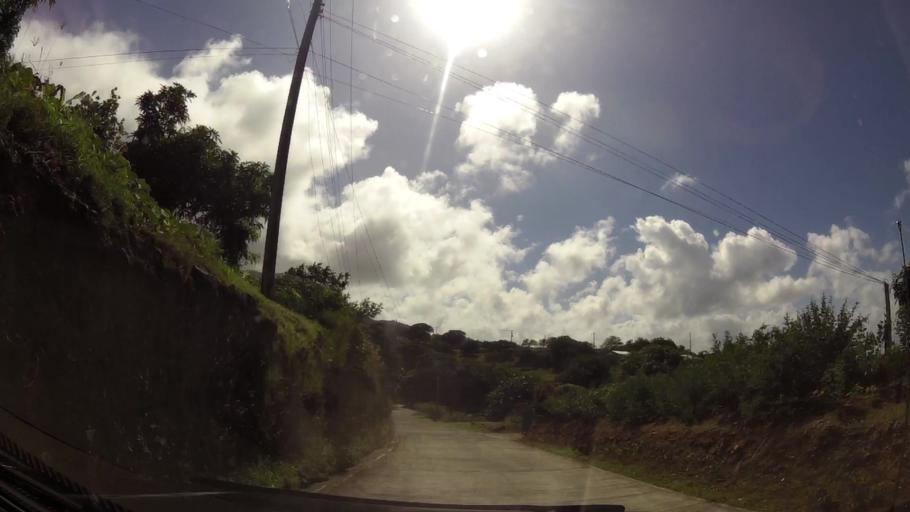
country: MS
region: Saint Peter
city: Brades
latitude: 16.7877
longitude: -62.2112
